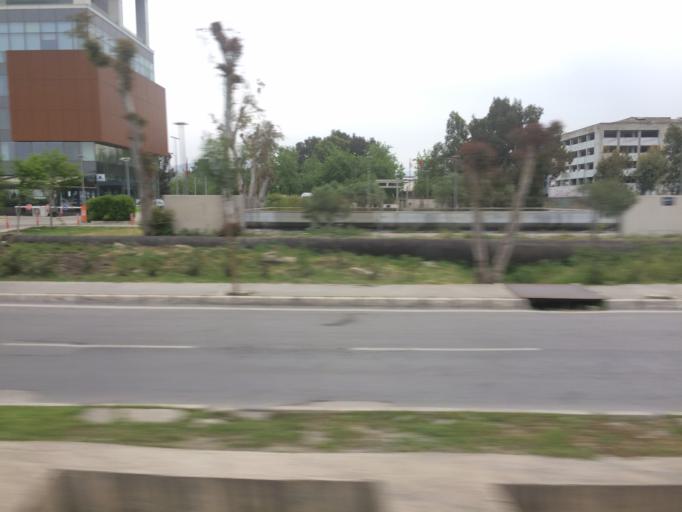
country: TR
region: Izmir
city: Izmir
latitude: 38.4561
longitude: 27.1674
